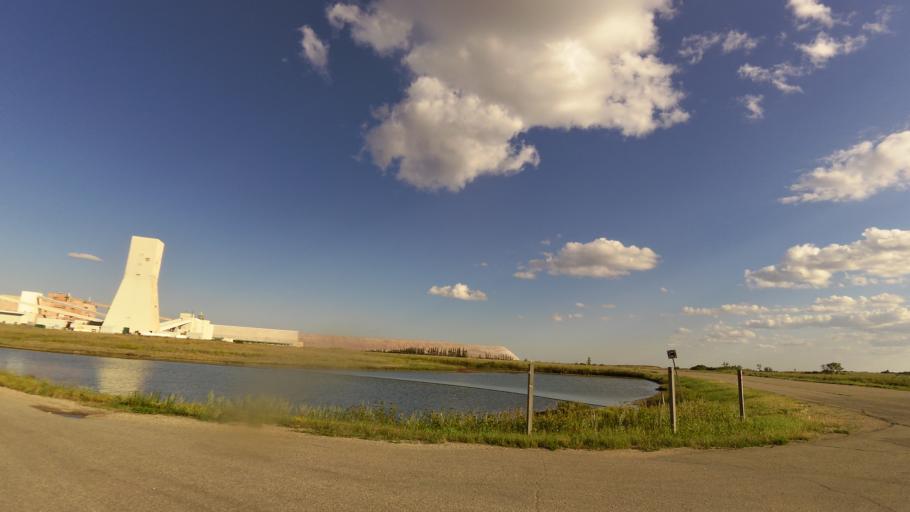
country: CA
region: Saskatchewan
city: Lanigan
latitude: 51.8557
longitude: -105.2165
